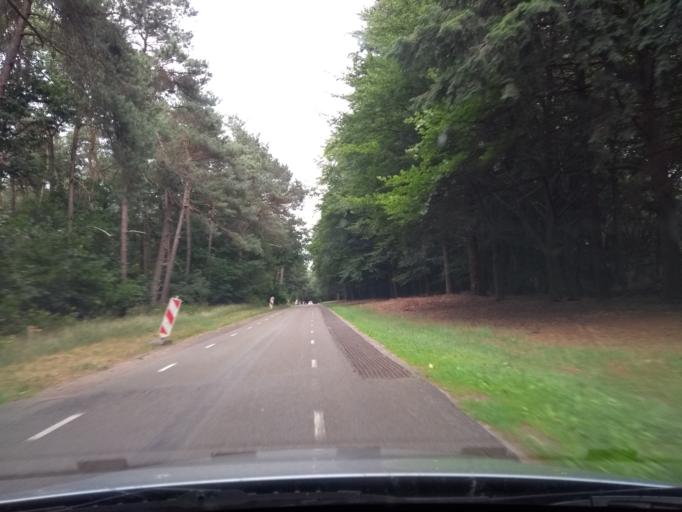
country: NL
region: Overijssel
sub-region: Gemeente Twenterand
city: Den Ham
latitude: 52.4576
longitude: 6.3989
